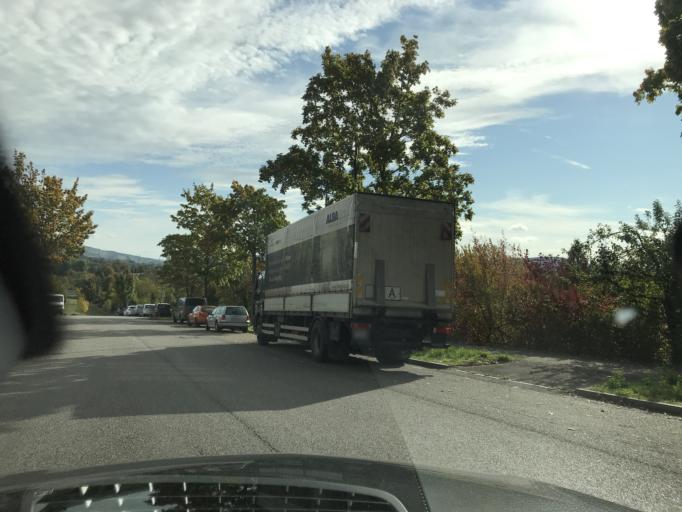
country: DE
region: Baden-Wuerttemberg
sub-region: Regierungsbezirk Stuttgart
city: Waiblingen
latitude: 48.8199
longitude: 9.3249
